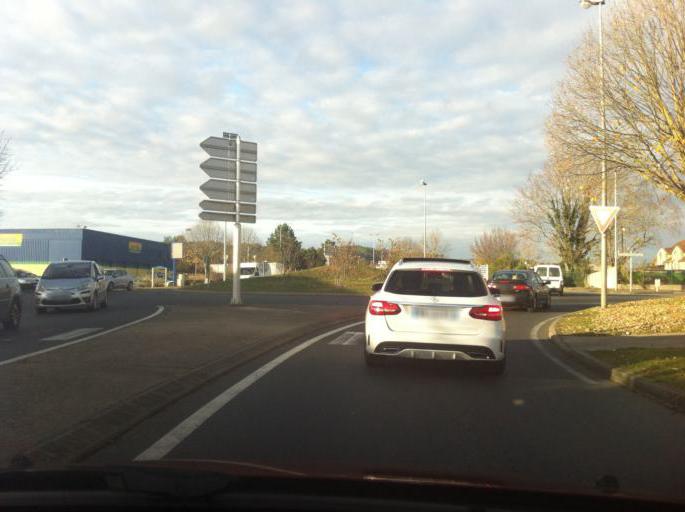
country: FR
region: Aquitaine
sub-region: Departement de la Dordogne
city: Chancelade
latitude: 45.1906
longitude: 0.6617
